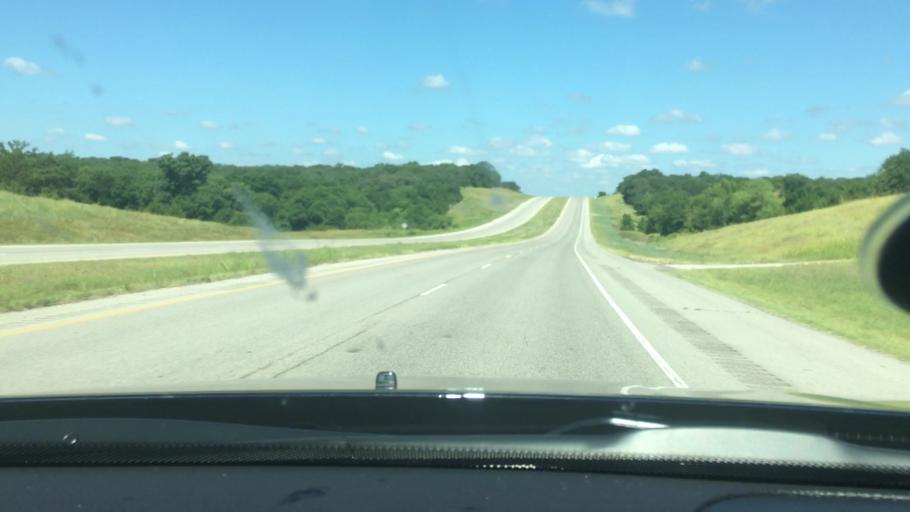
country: US
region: Oklahoma
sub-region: Carter County
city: Dickson
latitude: 34.1023
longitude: -96.9732
